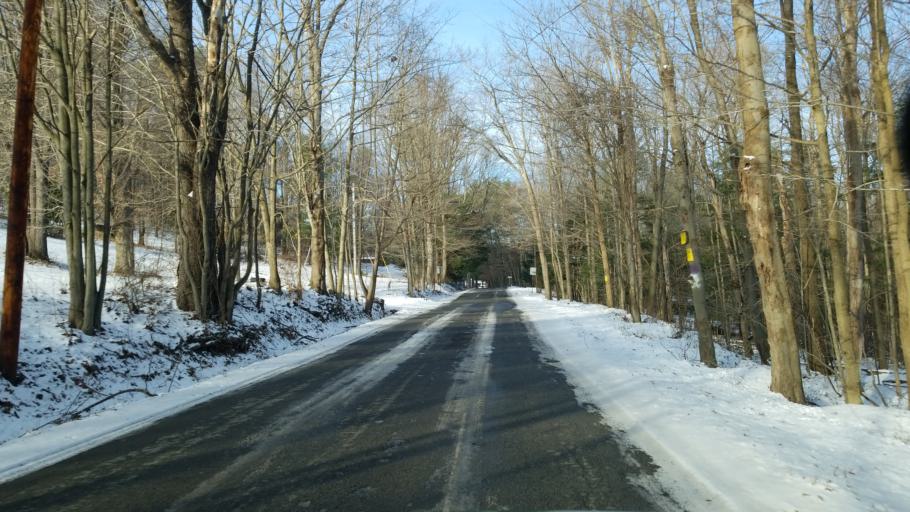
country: US
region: Pennsylvania
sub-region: Clearfield County
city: Treasure Lake
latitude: 41.0914
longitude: -78.6379
